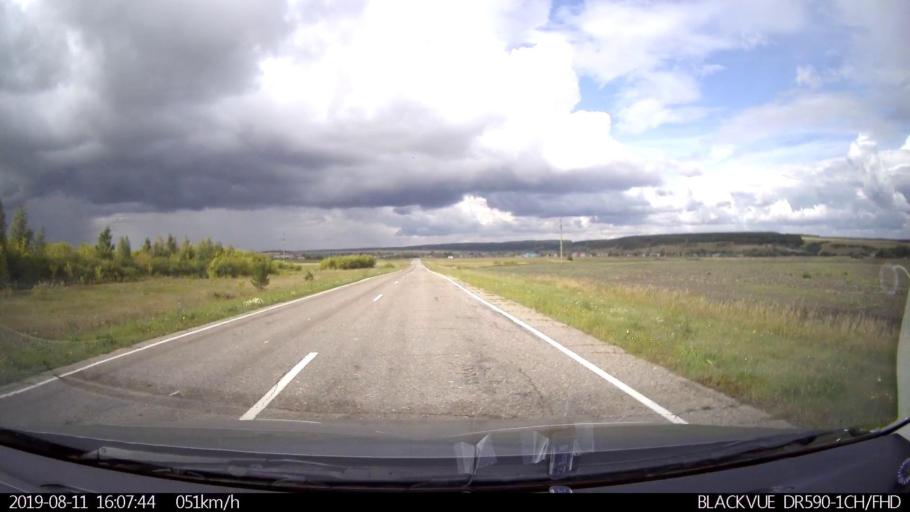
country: RU
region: Ulyanovsk
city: Ignatovka
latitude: 53.9794
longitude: 47.6466
